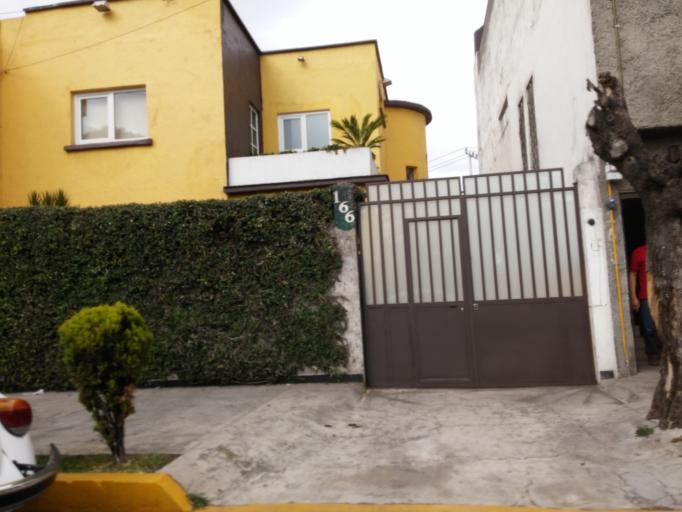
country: MX
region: Mexico City
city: Azcapotzalco
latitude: 19.4631
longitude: -99.1812
